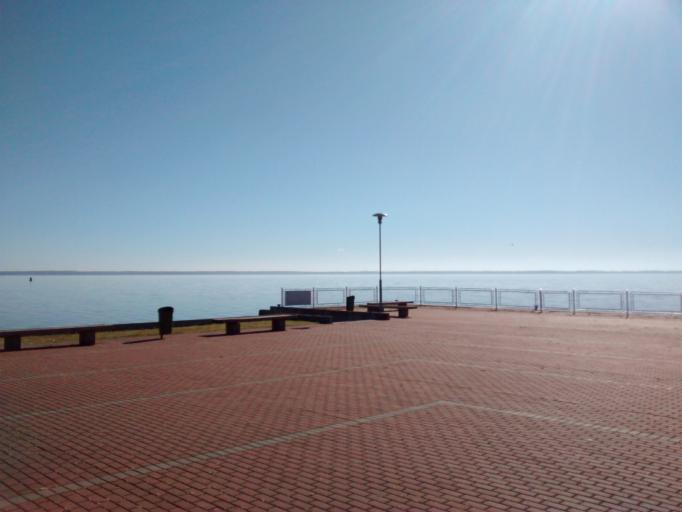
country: LT
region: Klaipedos apskritis
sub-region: Klaipeda
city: Klaipeda
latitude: 55.5420
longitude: 21.1226
